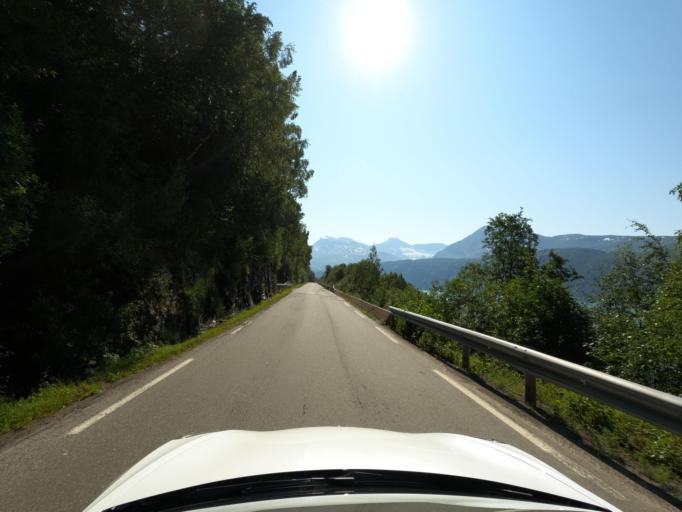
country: NO
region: Nordland
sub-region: Narvik
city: Narvik
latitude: 68.3464
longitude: 17.2795
